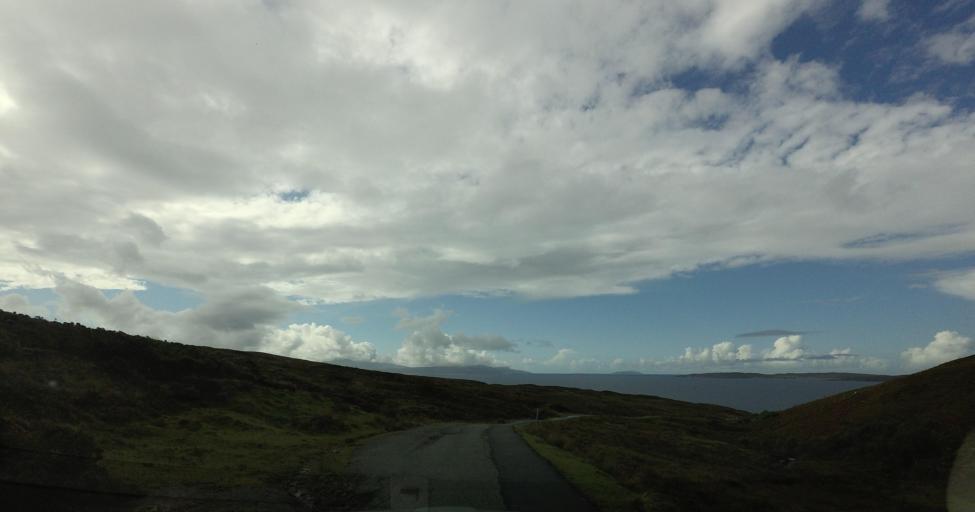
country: GB
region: Scotland
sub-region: Highland
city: Isle of Skye
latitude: 57.1458
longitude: -6.0962
